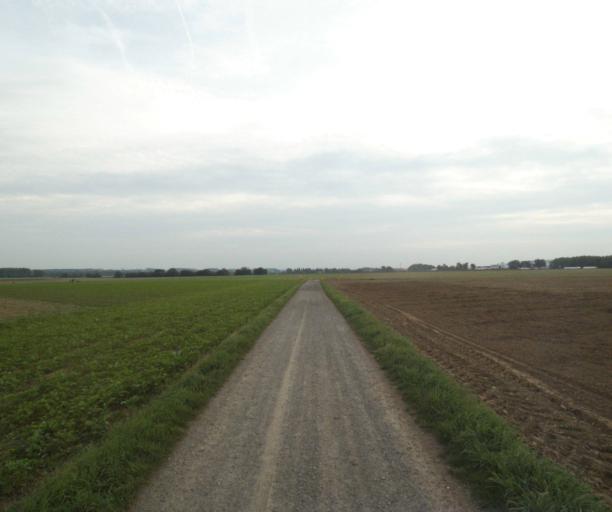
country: FR
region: Nord-Pas-de-Calais
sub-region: Departement du Nord
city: Avelin
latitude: 50.5572
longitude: 3.0697
